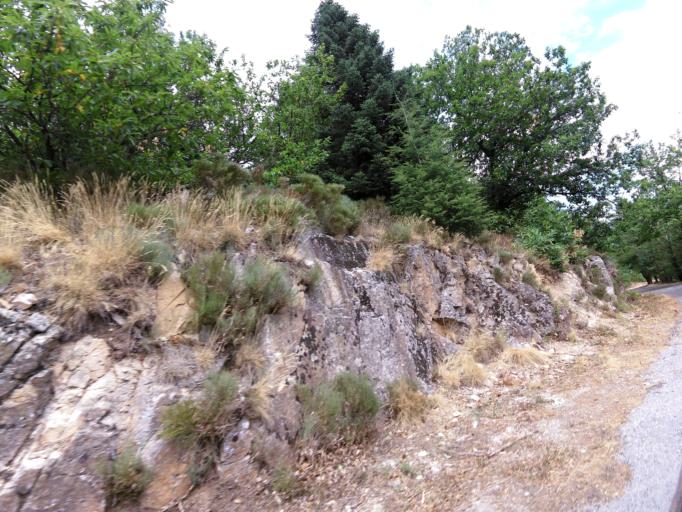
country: FR
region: Languedoc-Roussillon
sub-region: Departement du Gard
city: Le Vigan
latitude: 44.0360
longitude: 3.6101
